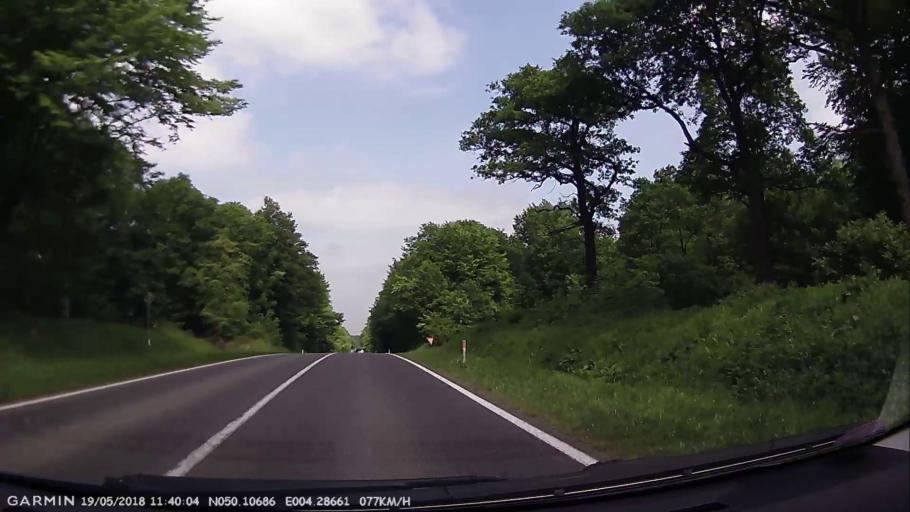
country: BE
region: Wallonia
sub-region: Province du Hainaut
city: Froidchapelle
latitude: 50.1070
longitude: 4.2866
